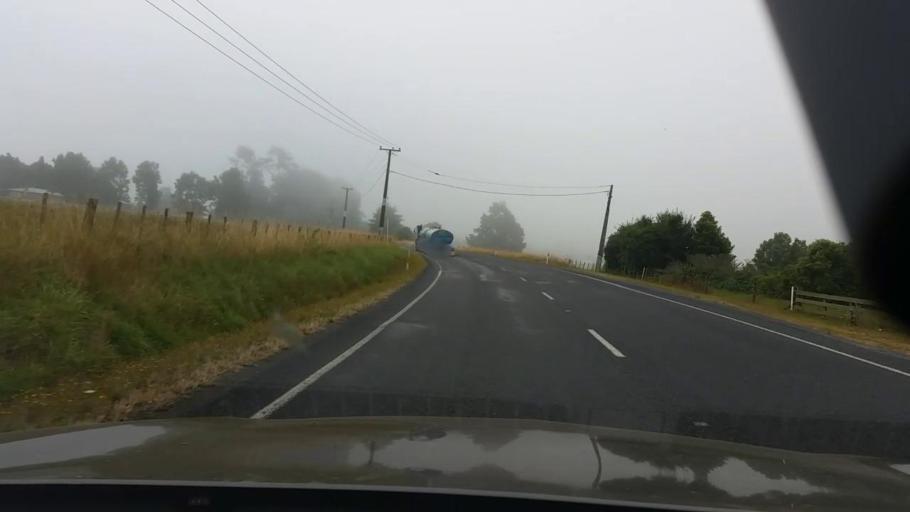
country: NZ
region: Waikato
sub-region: Hamilton City
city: Hamilton
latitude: -37.6446
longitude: 175.2956
